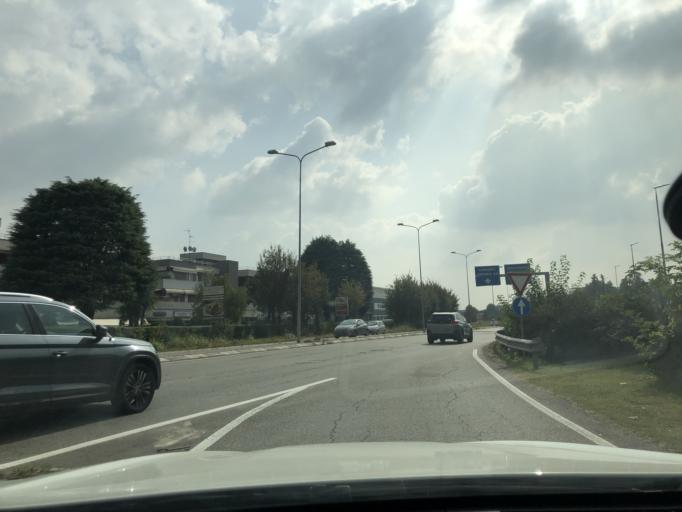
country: IT
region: Lombardy
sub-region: Citta metropolitana di Milano
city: Carugate
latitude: 45.5513
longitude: 9.3333
